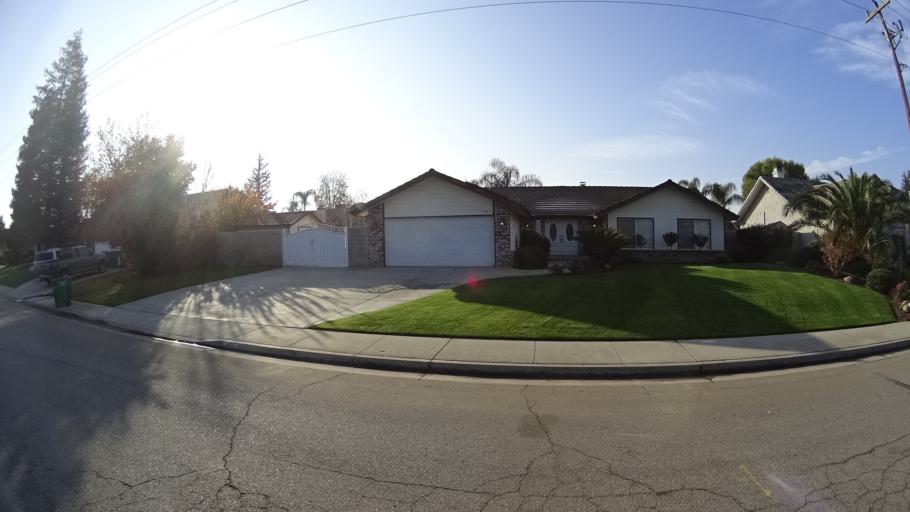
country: US
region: California
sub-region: Kern County
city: Rosedale
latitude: 35.3762
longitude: -119.1653
